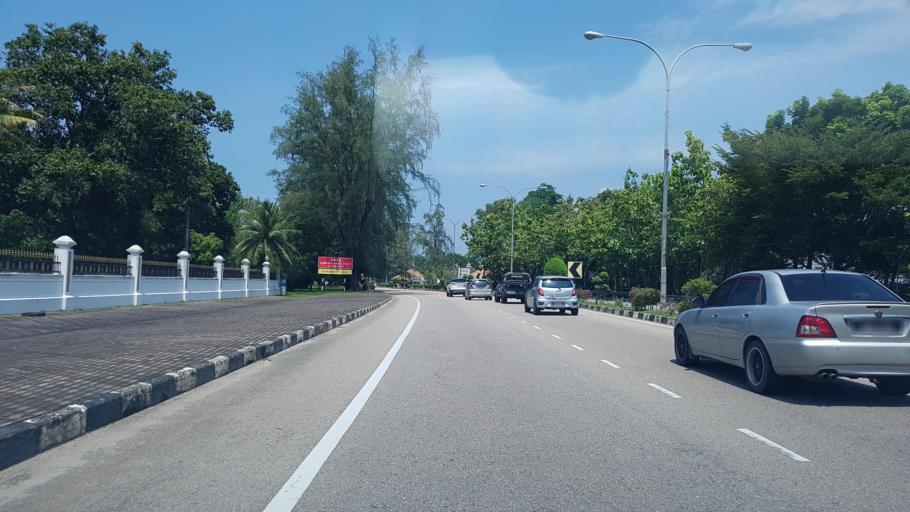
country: MY
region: Terengganu
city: Kuala Terengganu
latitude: 5.3028
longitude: 103.1613
